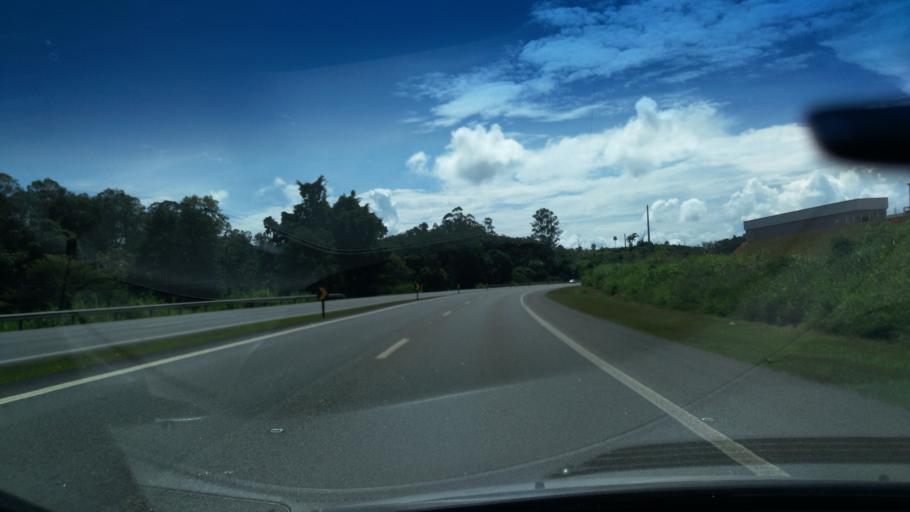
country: BR
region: Sao Paulo
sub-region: Santo Antonio Do Jardim
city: Espirito Santo do Pinhal
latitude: -22.2240
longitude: -46.7930
